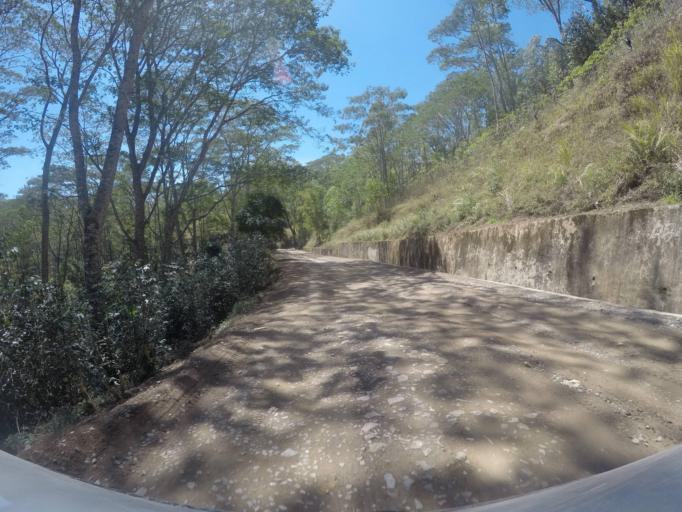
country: TL
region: Ermera
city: Gleno
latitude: -8.7816
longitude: 125.3790
